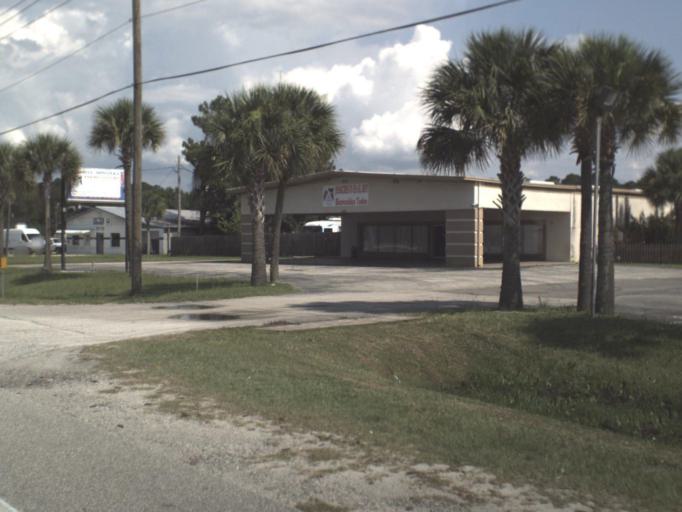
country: US
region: Florida
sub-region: Putnam County
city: Palatka
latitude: 29.6574
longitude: -81.6662
